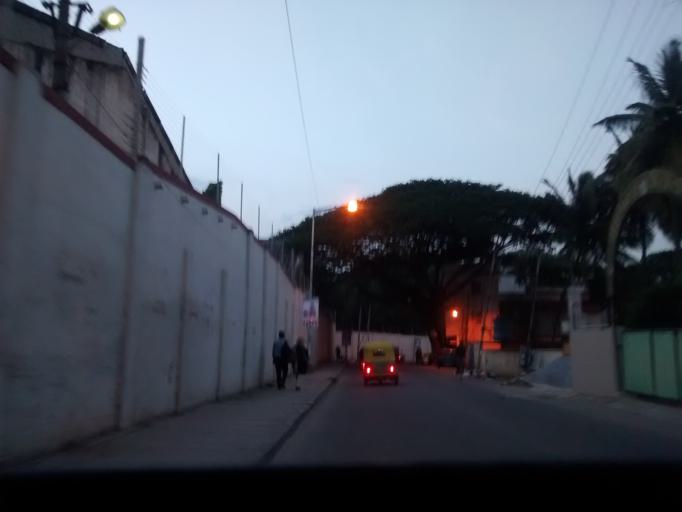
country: IN
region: Karnataka
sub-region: Bangalore Urban
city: Bangalore
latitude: 12.9722
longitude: 77.6616
